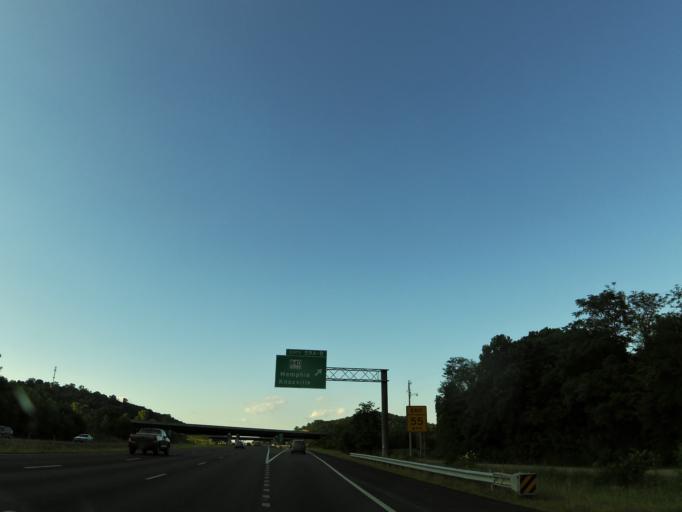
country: US
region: Tennessee
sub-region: Williamson County
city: Thompson's Station
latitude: 35.8164
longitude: -86.8422
